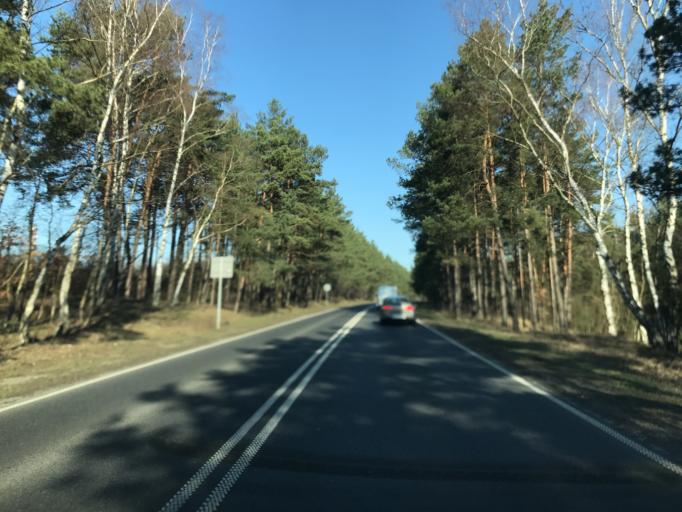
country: PL
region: Kujawsko-Pomorskie
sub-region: Bydgoszcz
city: Fordon
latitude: 53.0812
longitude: 18.1221
